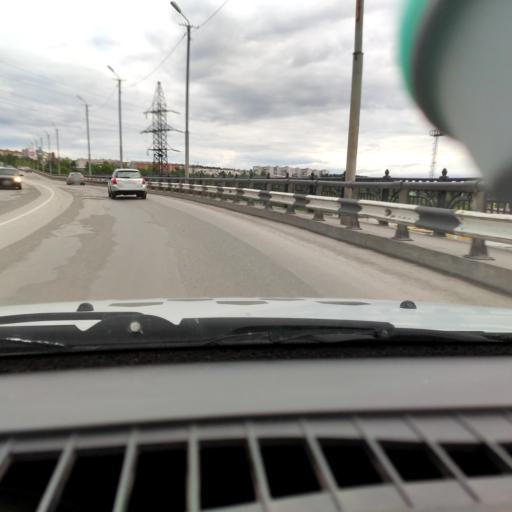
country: RU
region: Perm
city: Chusovoy
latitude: 58.2888
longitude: 57.8123
